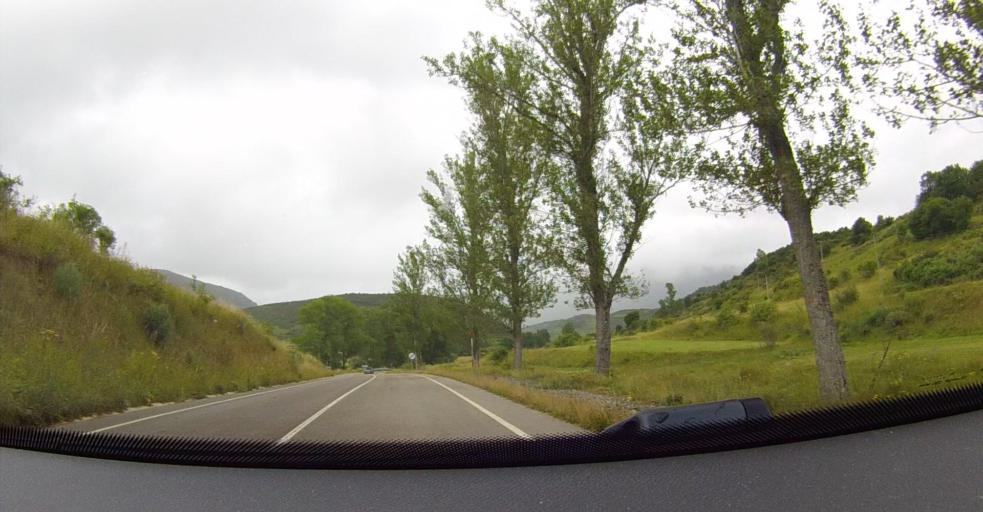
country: ES
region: Castille and Leon
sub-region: Provincia de Leon
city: Acebedo
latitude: 43.0582
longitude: -5.1342
